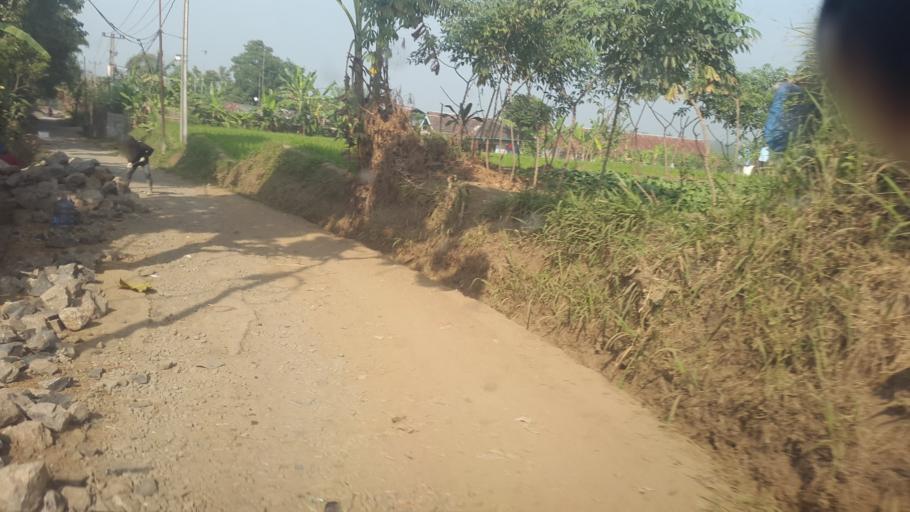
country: ID
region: West Java
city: Sukabumi
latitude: -6.8885
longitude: 106.9892
